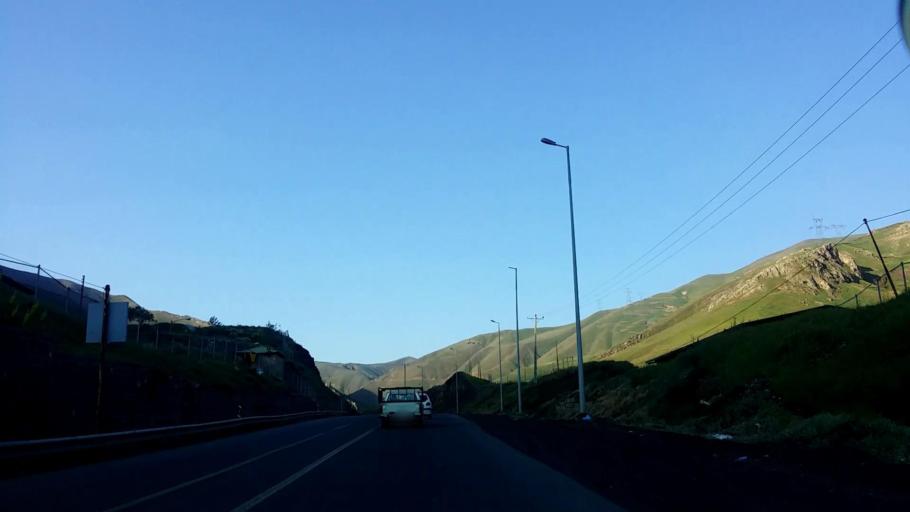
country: IR
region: Tehran
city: Tajrish
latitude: 36.1935
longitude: 51.3202
